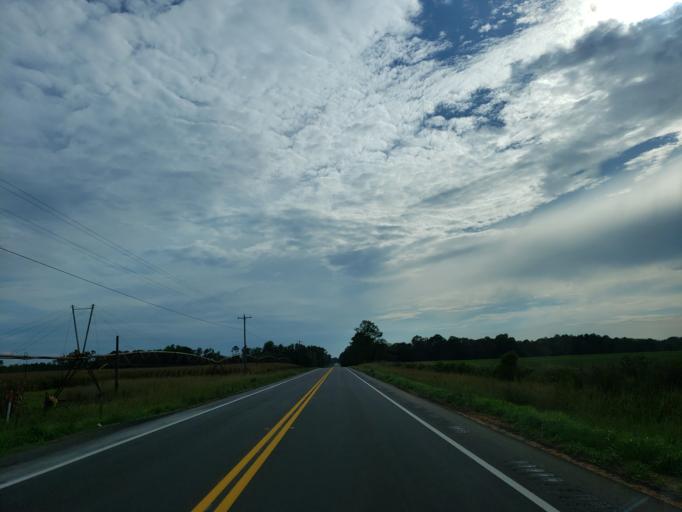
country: US
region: Georgia
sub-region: Irwin County
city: Ocilla
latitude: 31.5894
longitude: -83.2700
